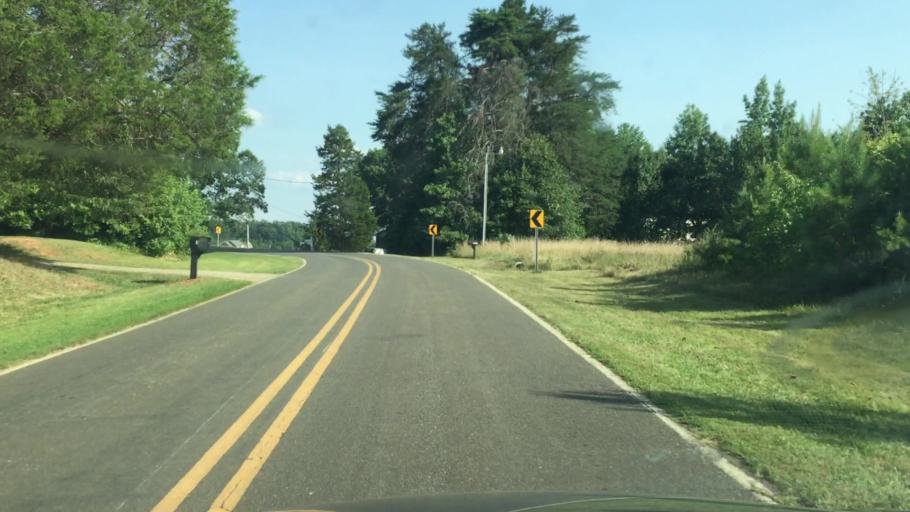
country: US
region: North Carolina
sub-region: Rockingham County
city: Reidsville
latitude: 36.2713
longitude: -79.5659
